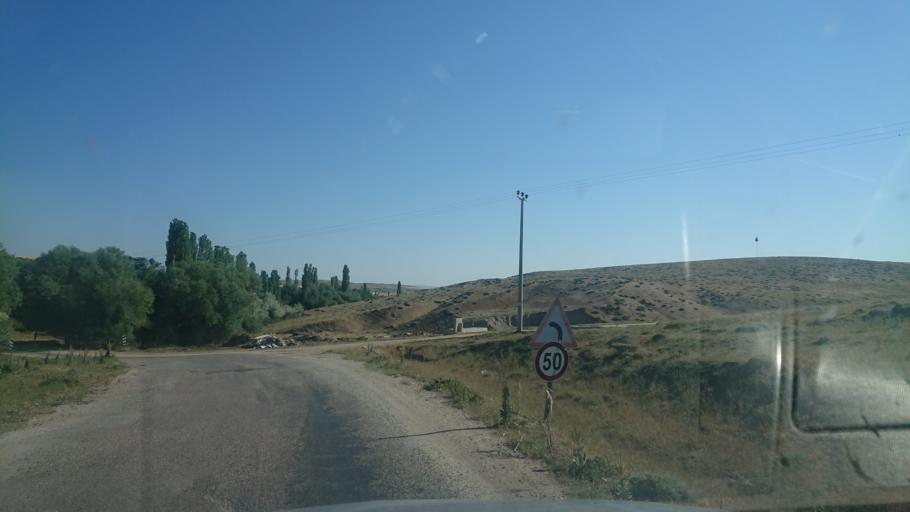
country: TR
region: Aksaray
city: Agacoren
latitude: 38.8790
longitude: 33.8811
